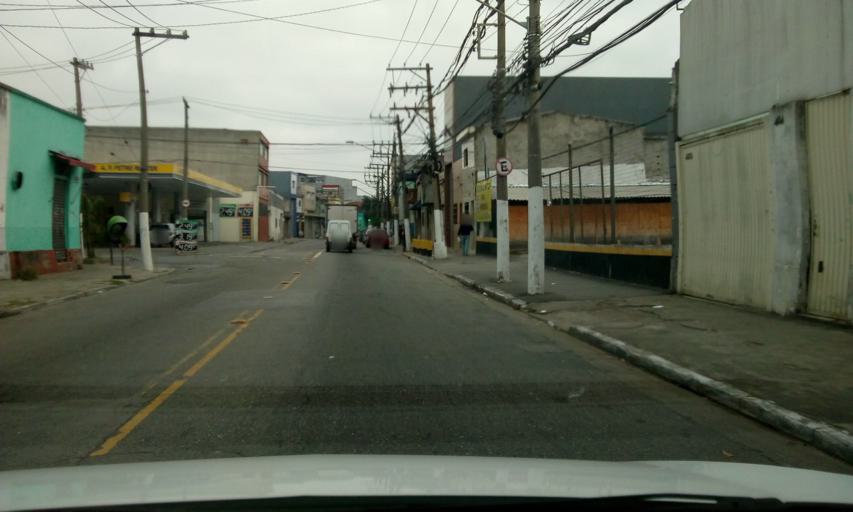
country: BR
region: Sao Paulo
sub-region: Sao Paulo
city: Sao Paulo
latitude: -23.5346
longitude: -46.6030
